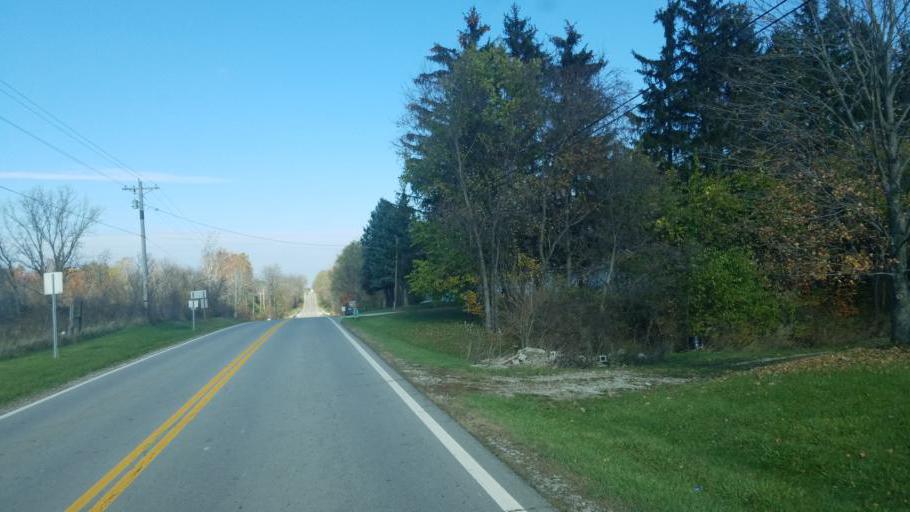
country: US
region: Ohio
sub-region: Lorain County
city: Wellington
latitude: 41.1309
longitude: -82.3060
